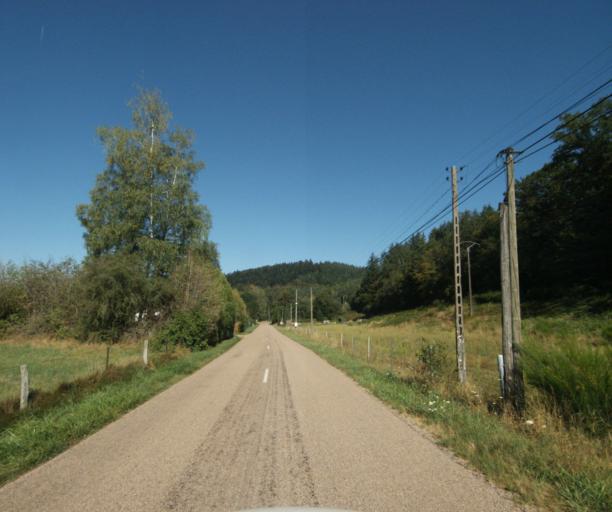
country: FR
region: Lorraine
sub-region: Departement des Vosges
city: Arches
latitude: 48.1464
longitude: 6.5028
